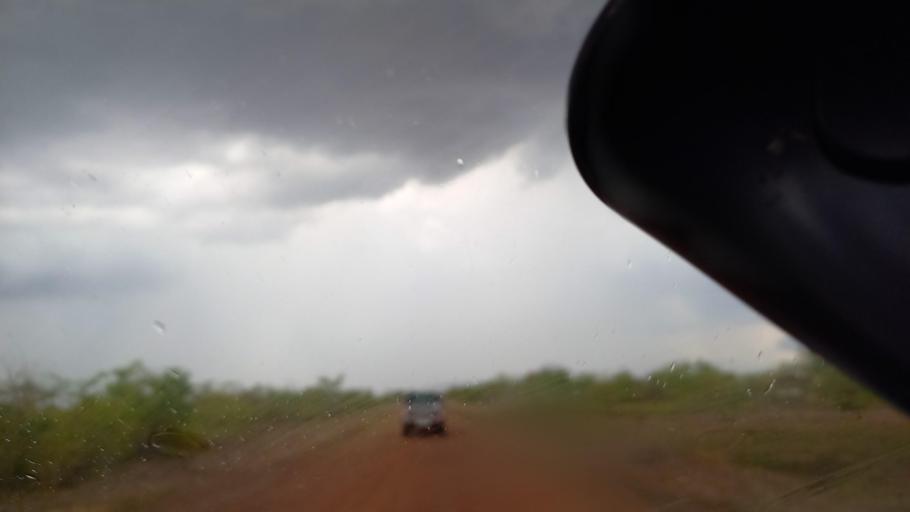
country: ZM
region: Lusaka
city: Kafue
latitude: -15.8652
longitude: 28.1811
